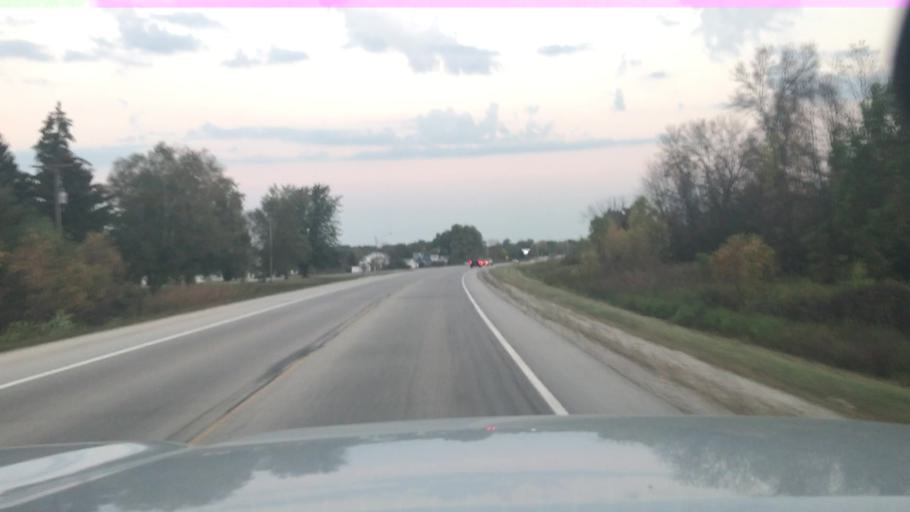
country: US
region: Wisconsin
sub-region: Brown County
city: Bellevue
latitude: 44.4547
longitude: -87.9448
